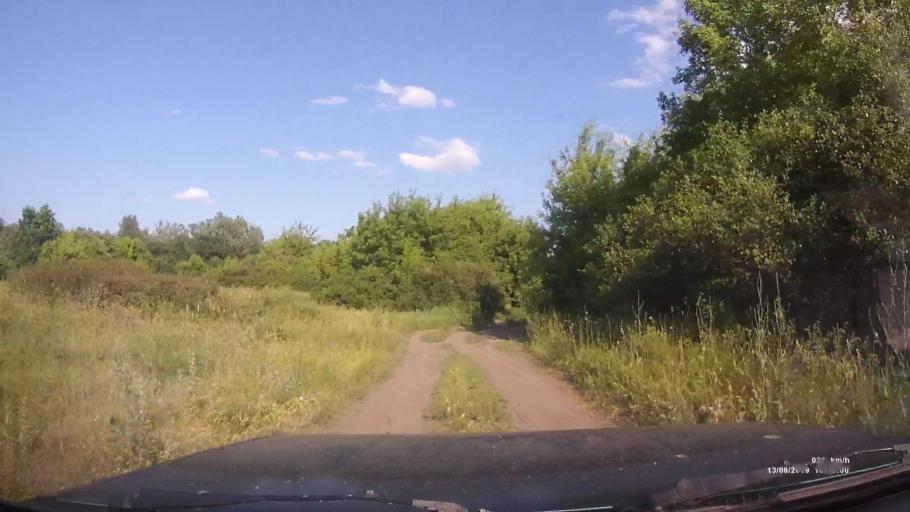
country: RU
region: Rostov
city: Kazanskaya
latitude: 49.9464
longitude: 41.4254
